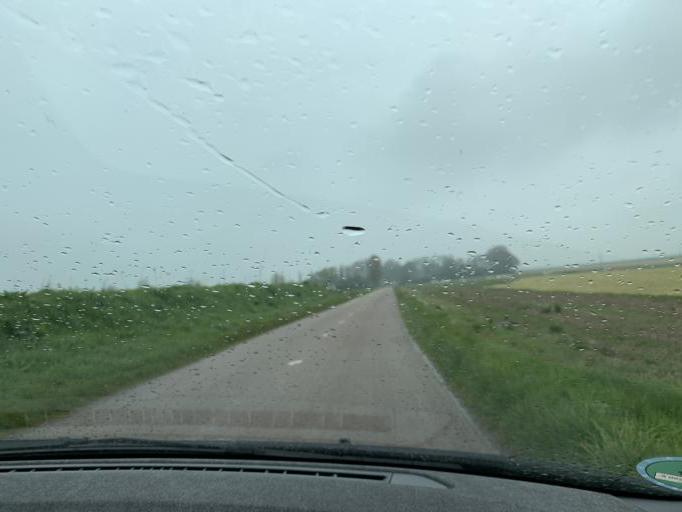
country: FR
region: Haute-Normandie
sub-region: Departement de la Seine-Maritime
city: Les Loges
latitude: 49.7183
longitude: 0.2554
